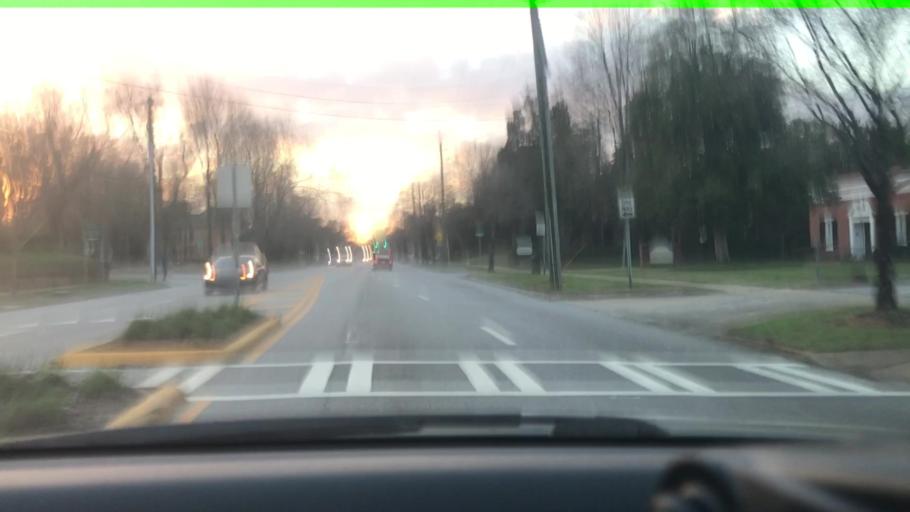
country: US
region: Georgia
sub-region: Clarke County
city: Athens
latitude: 33.9611
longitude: -83.3873
